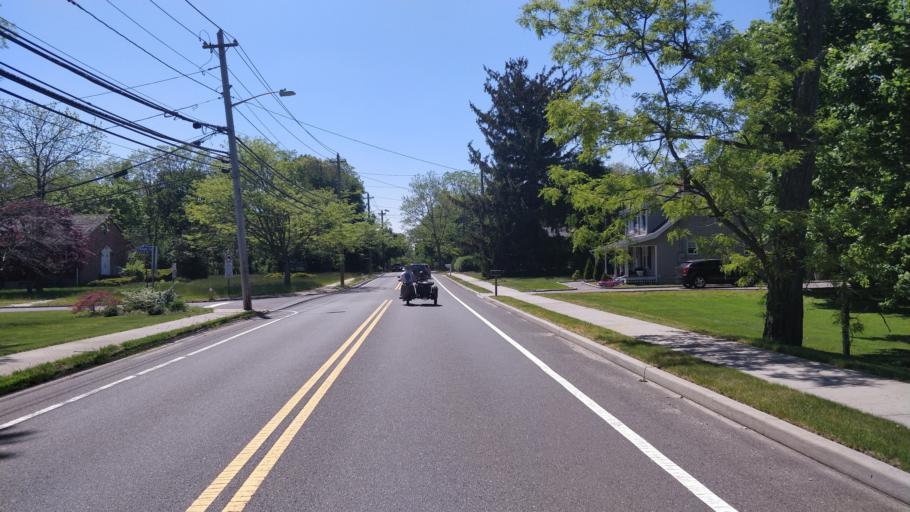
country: US
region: New York
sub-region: Suffolk County
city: Hauppauge
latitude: 40.8263
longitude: -73.1886
